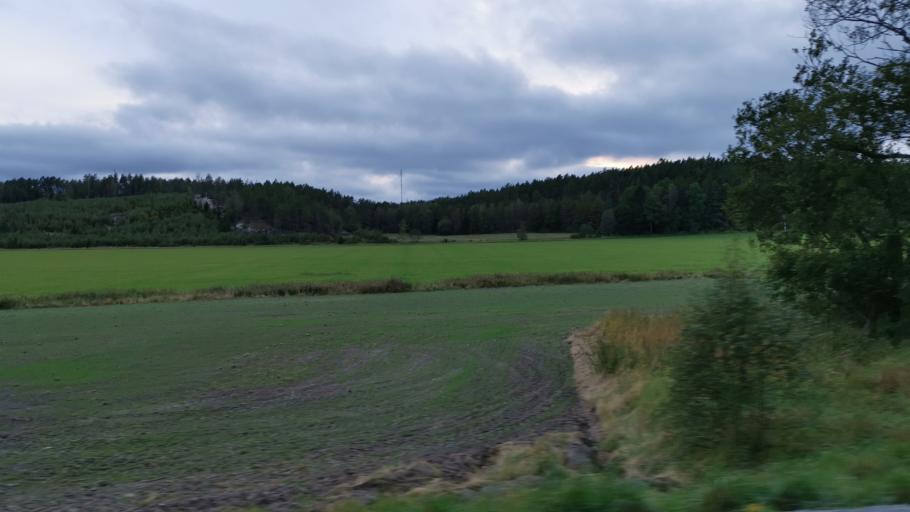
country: SE
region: Vaestra Goetaland
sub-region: Tanums Kommun
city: Tanumshede
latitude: 58.6830
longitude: 11.3369
